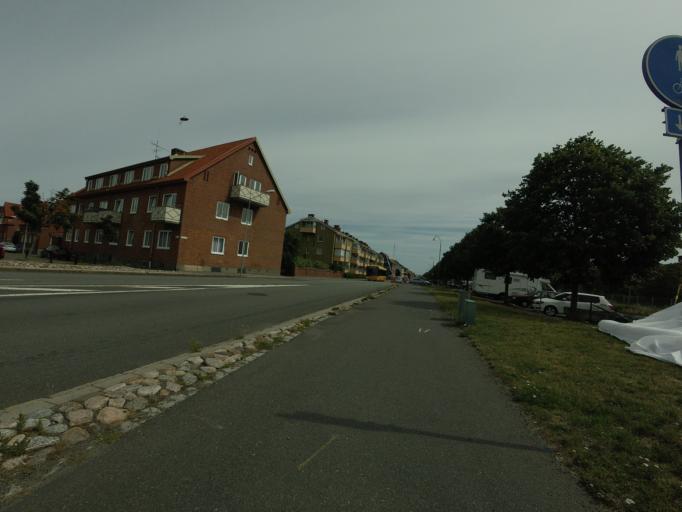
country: SE
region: Skane
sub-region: Simrishamns Kommun
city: Simrishamn
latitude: 55.5532
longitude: 14.3483
